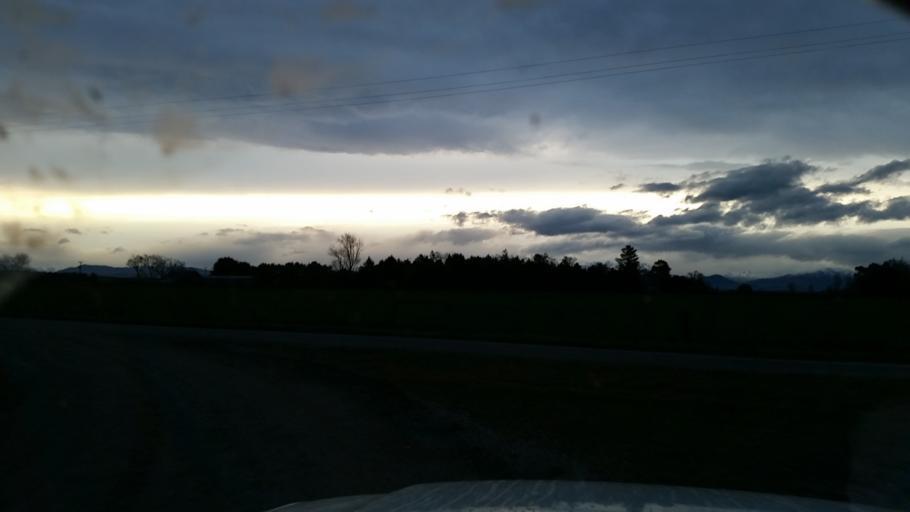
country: NZ
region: Canterbury
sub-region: Ashburton District
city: Ashburton
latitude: -43.8502
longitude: 171.6455
